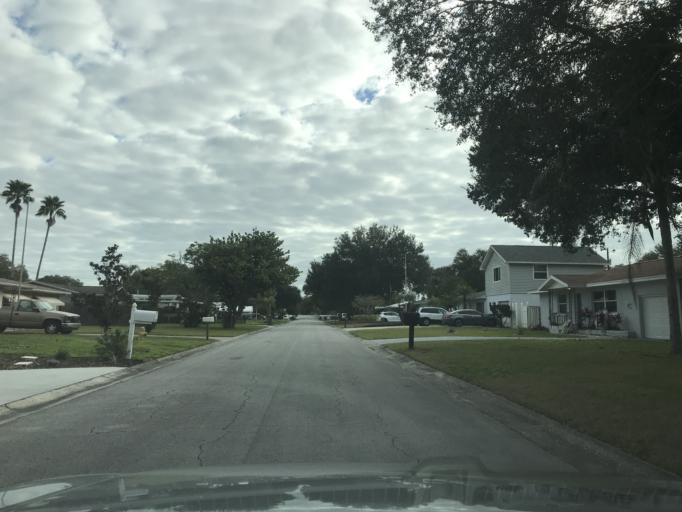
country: US
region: Florida
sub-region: Pinellas County
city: Belleair
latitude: 27.9439
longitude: -82.7775
